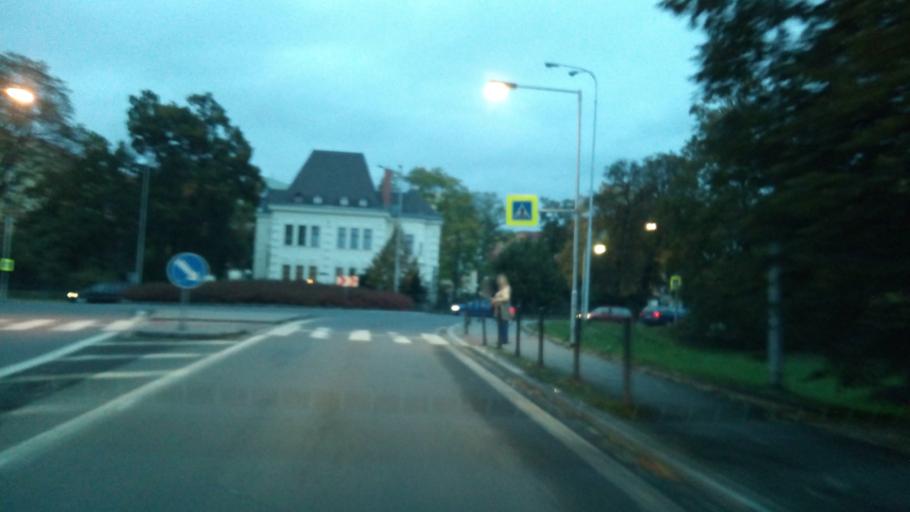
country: CZ
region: Moravskoslezsky
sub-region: Okres Frydek-Mistek
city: Stare Mesto
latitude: 49.6777
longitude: 18.3583
